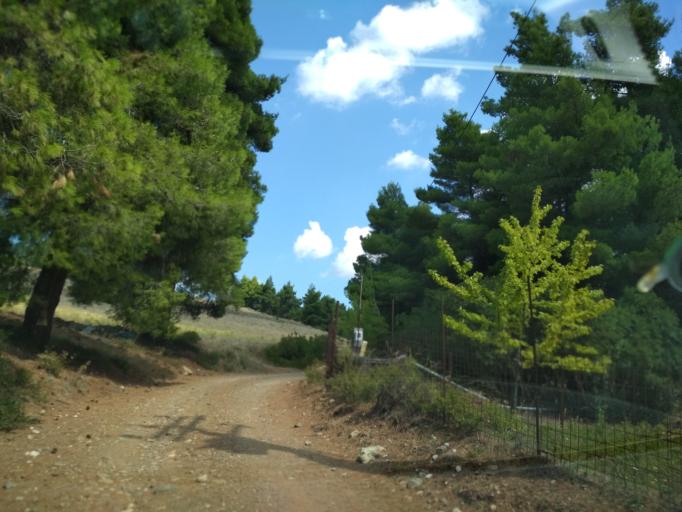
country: GR
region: Central Greece
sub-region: Nomos Evvoias
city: Roviai
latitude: 38.8374
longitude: 23.2788
